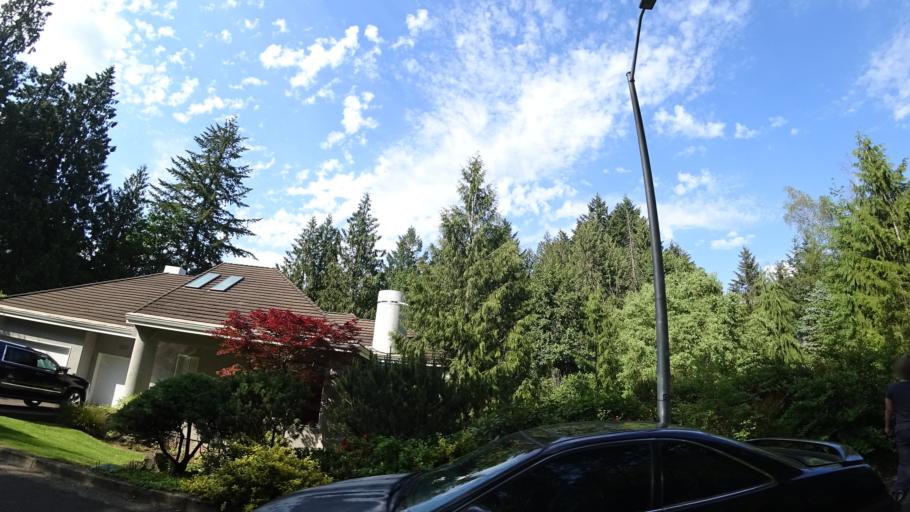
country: US
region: Oregon
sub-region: Washington County
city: Garden Home-Whitford
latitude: 45.4580
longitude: -122.7348
